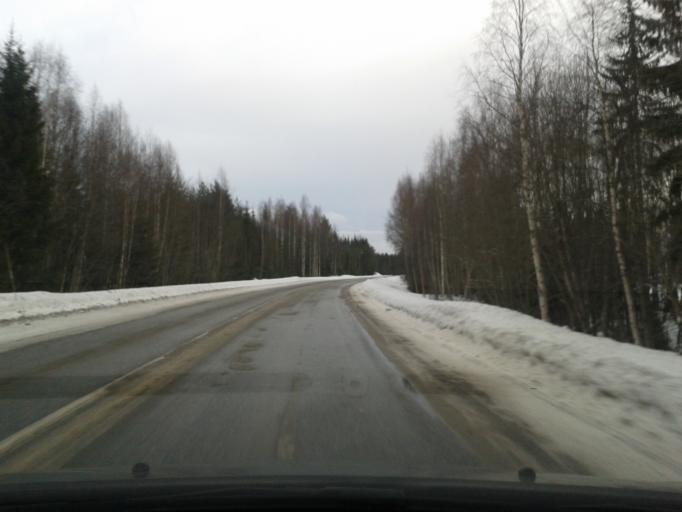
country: SE
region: Vaesternorrland
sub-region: Solleftea Kommun
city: As
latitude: 63.6593
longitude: 16.7871
